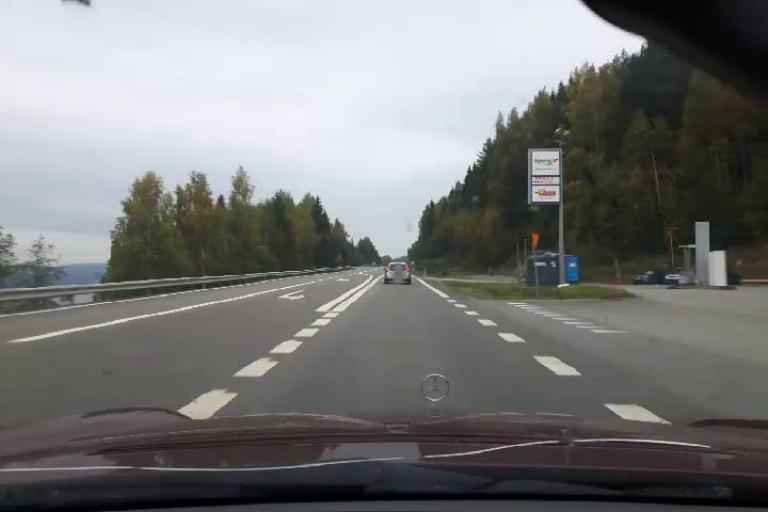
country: SE
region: Vaesternorrland
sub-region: Kramfors Kommun
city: Nordingra
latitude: 63.0408
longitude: 18.3264
